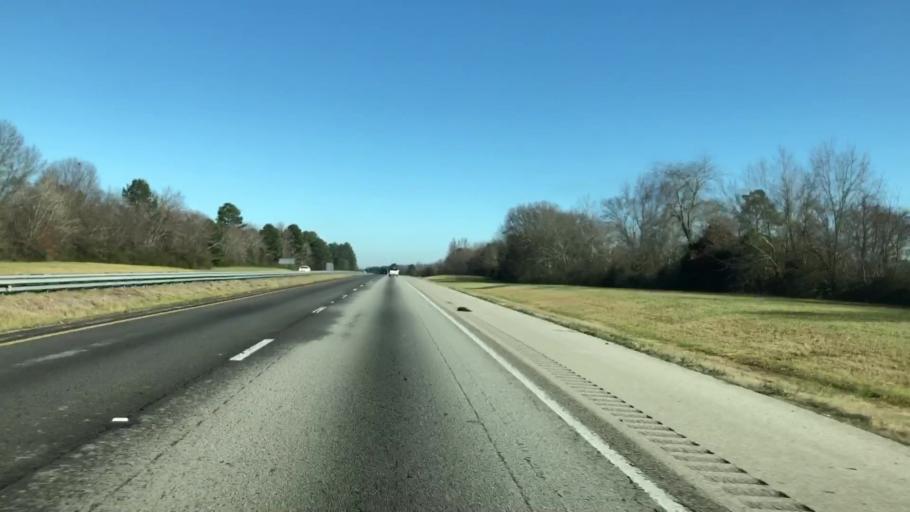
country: US
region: Alabama
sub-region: Limestone County
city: Athens
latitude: 34.8451
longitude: -86.9326
